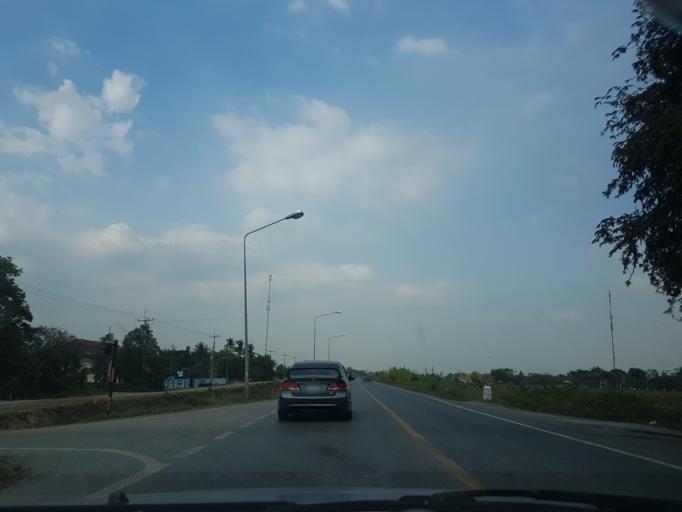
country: TH
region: Sara Buri
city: Nong Saeng
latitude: 14.5054
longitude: 100.7348
